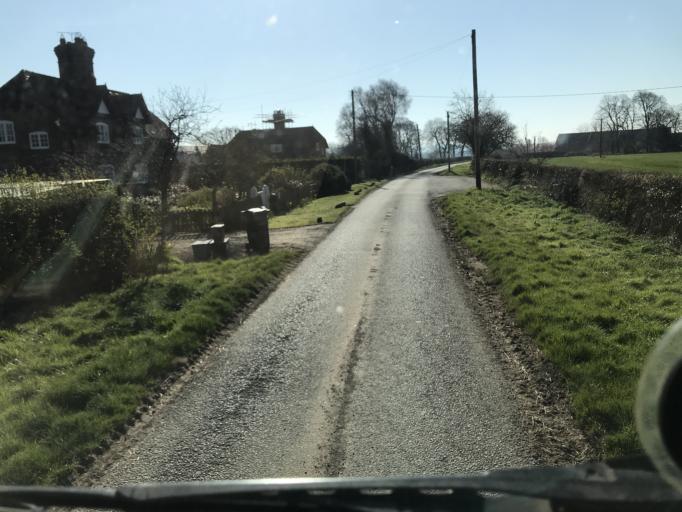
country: GB
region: England
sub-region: Cheshire West and Chester
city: Aldford
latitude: 53.1261
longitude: -2.8525
